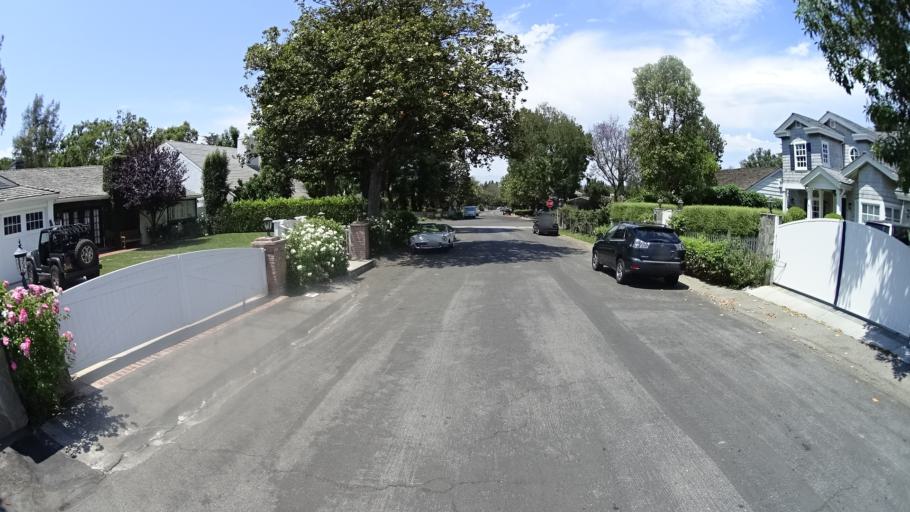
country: US
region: California
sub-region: Los Angeles County
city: Sherman Oaks
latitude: 34.1431
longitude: -118.4197
